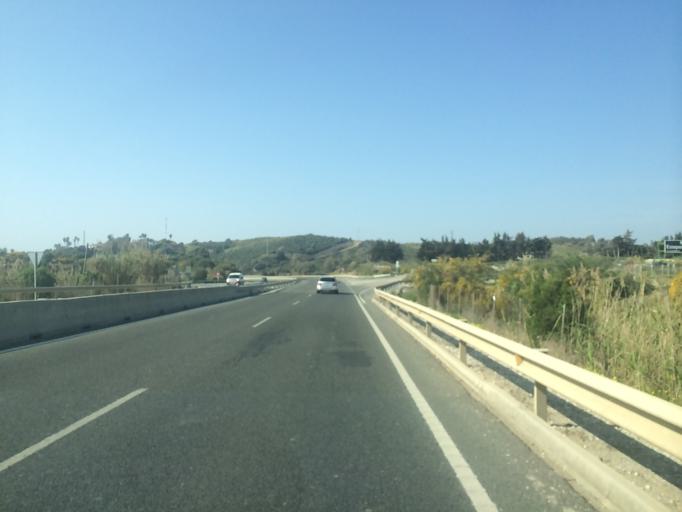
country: ES
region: Andalusia
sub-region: Provincia de Malaga
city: Estepona
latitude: 36.4052
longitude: -5.1925
